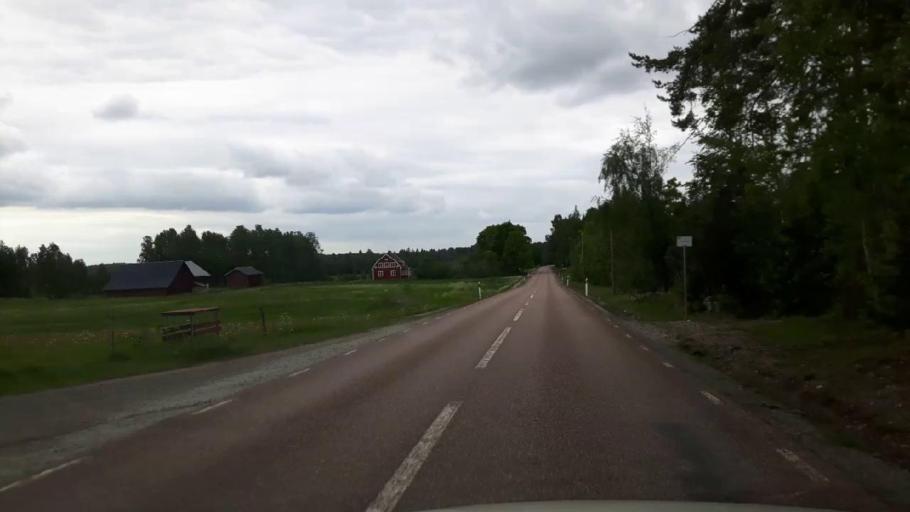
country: SE
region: Vaestmanland
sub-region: Kopings Kommun
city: Kolsva
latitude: 59.6901
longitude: 15.7745
